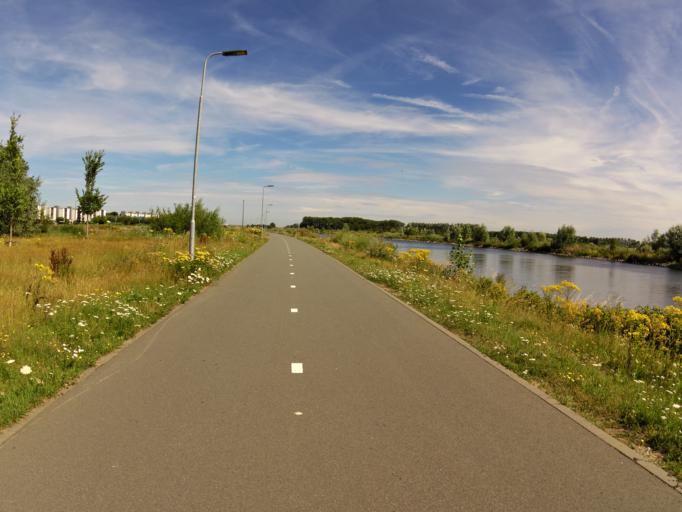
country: NL
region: North Brabant
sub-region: Gemeente 's-Hertogenbosch
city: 's-Hertogenbosch
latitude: 51.7309
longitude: 5.3386
